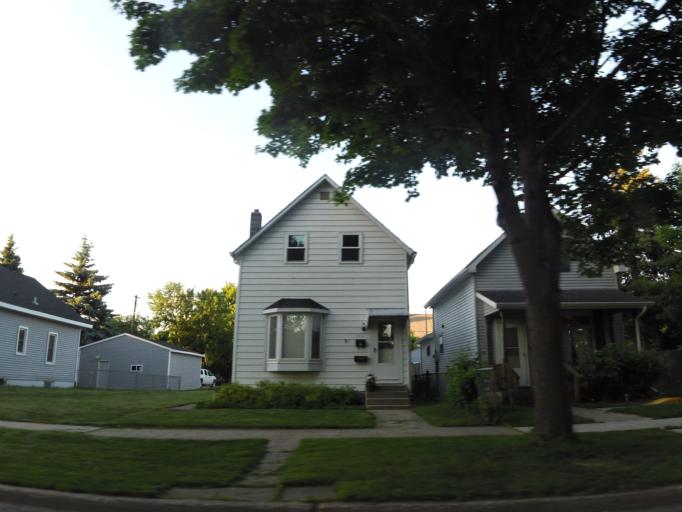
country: US
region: North Dakota
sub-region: Grand Forks County
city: Grand Forks
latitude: 47.9259
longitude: -97.0410
